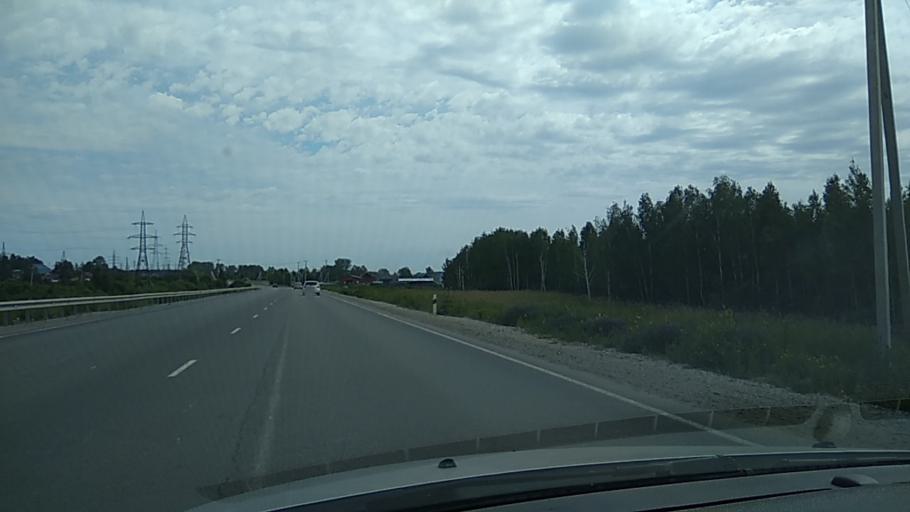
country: RU
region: Sverdlovsk
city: Verkhnyaya Pyshma
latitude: 56.9494
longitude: 60.5939
